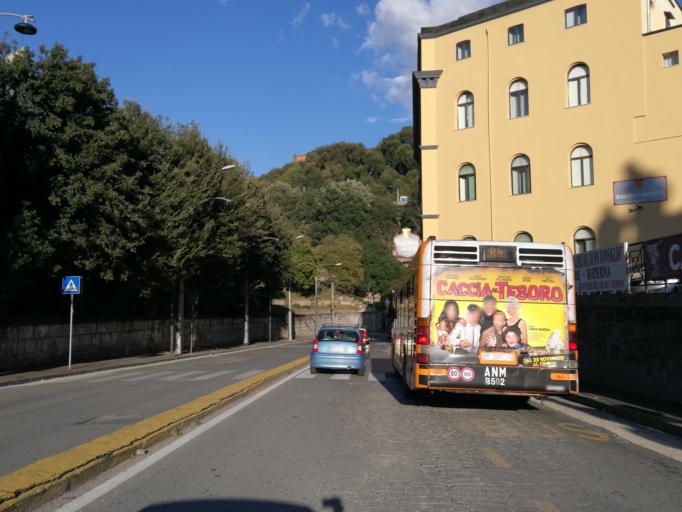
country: IT
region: Campania
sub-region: Provincia di Napoli
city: Napoli
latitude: 40.8654
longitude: 14.2471
